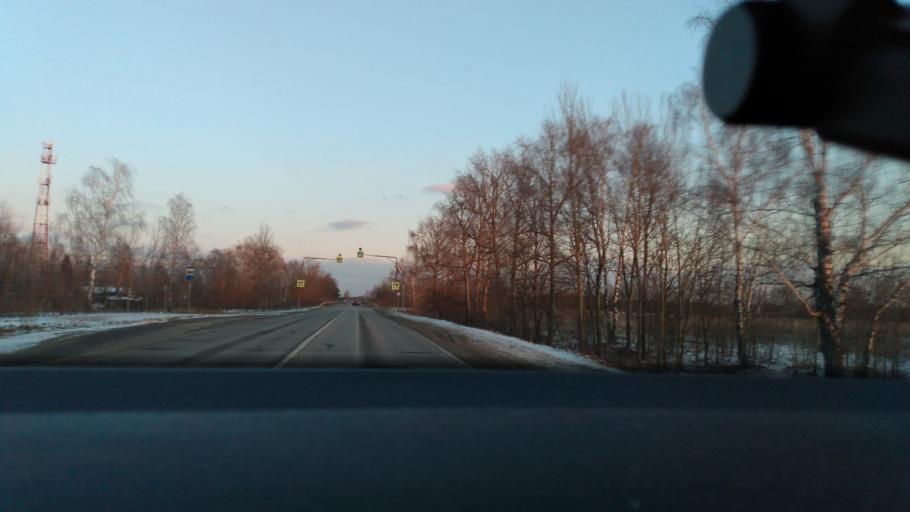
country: RU
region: Moskovskaya
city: Kolomna
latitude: 55.0882
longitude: 38.9153
